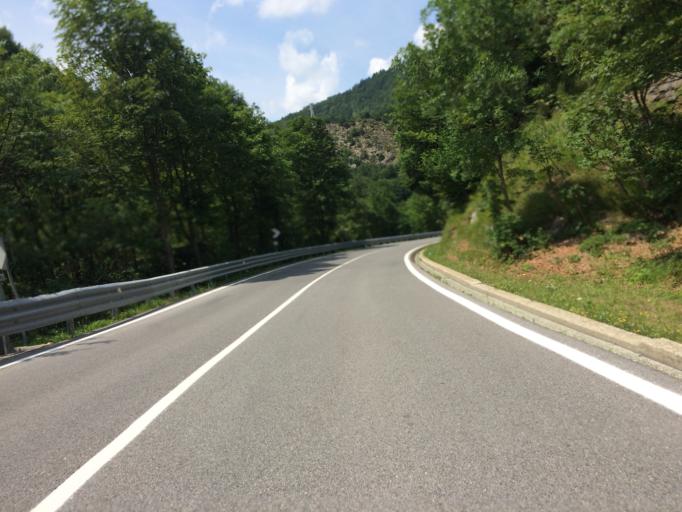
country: IT
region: Piedmont
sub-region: Provincia di Cuneo
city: Limone Piemonte
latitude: 44.2260
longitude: 7.5628
